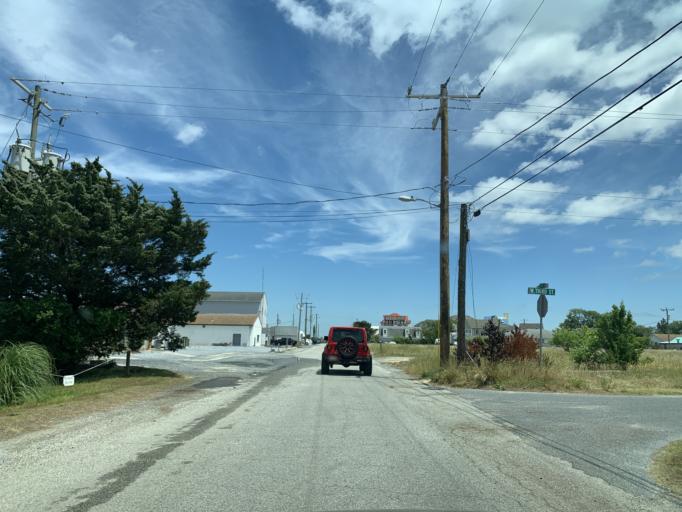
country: US
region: Maryland
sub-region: Worcester County
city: West Ocean City
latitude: 38.3265
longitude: -75.1047
